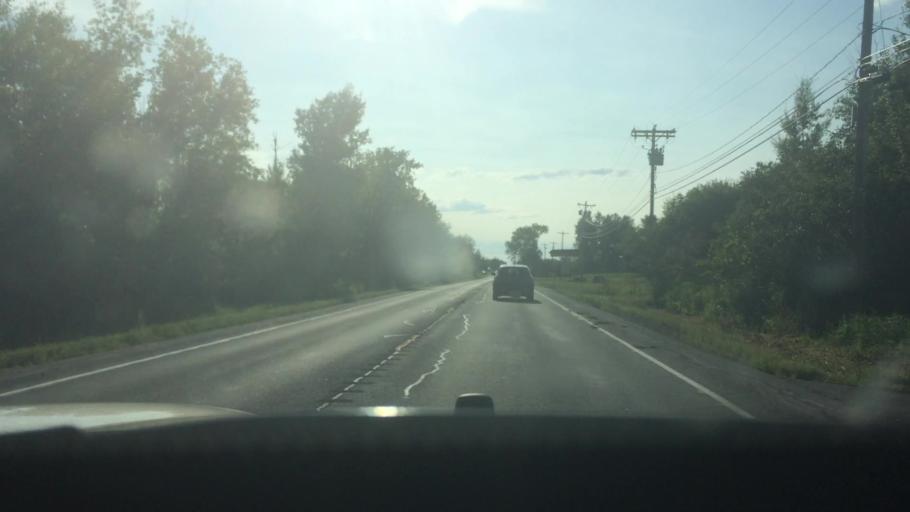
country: US
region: New York
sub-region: St. Lawrence County
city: Potsdam
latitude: 44.6700
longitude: -74.9439
